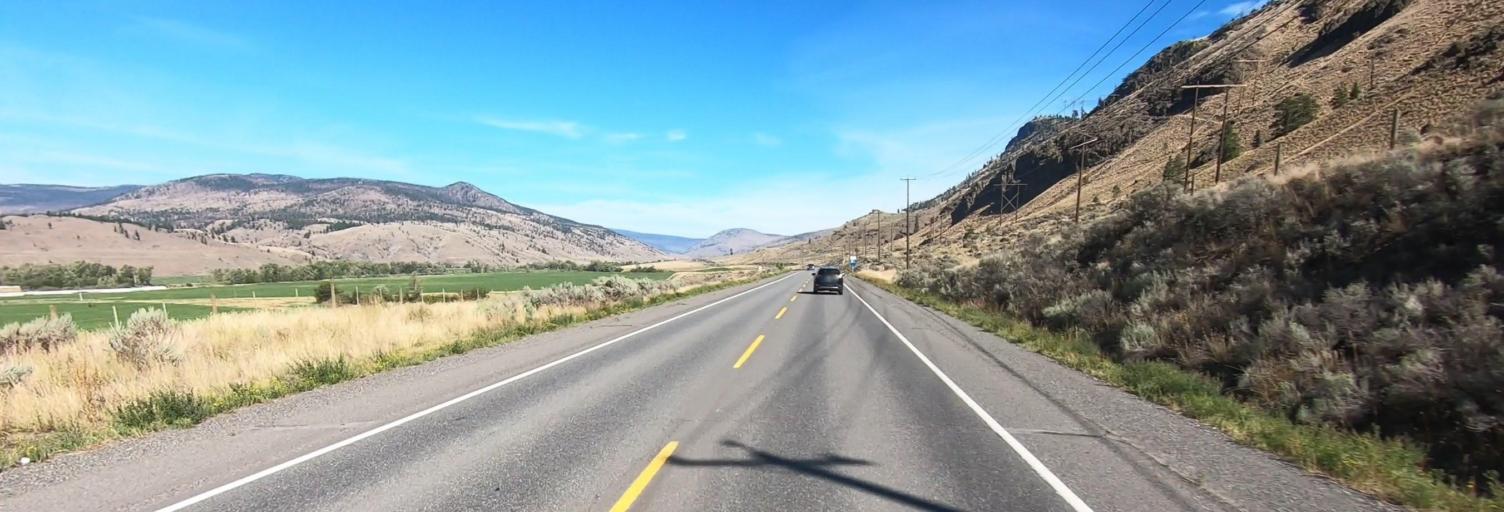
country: CA
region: British Columbia
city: Cache Creek
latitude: 50.8703
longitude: -121.3920
